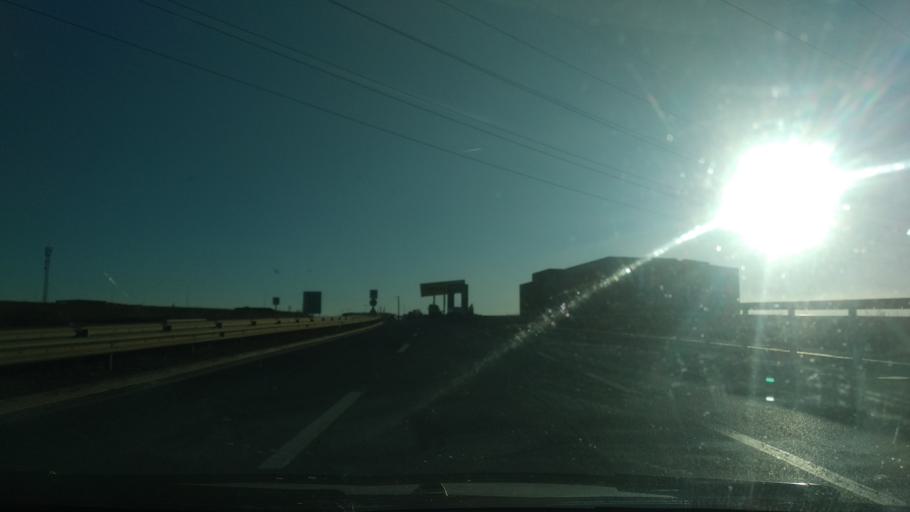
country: XK
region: Pristina
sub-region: Kosovo Polje
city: Kosovo Polje
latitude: 42.6806
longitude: 21.1161
